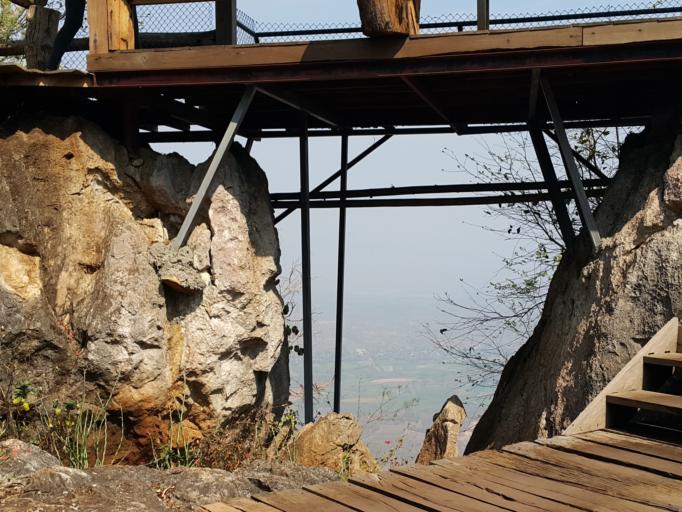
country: TH
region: Lampang
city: Mueang Pan
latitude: 18.7458
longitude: 99.5321
